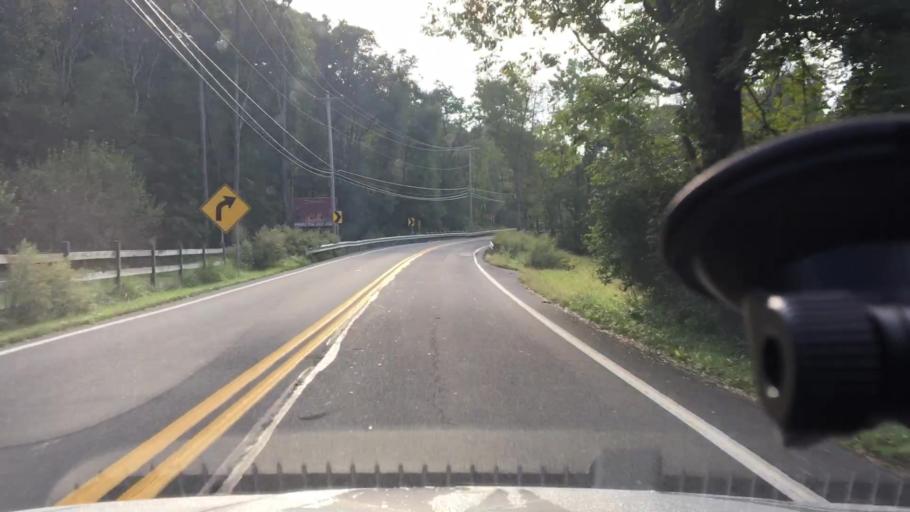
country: US
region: Pennsylvania
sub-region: Monroe County
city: Mount Pocono
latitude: 41.0984
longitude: -75.3348
